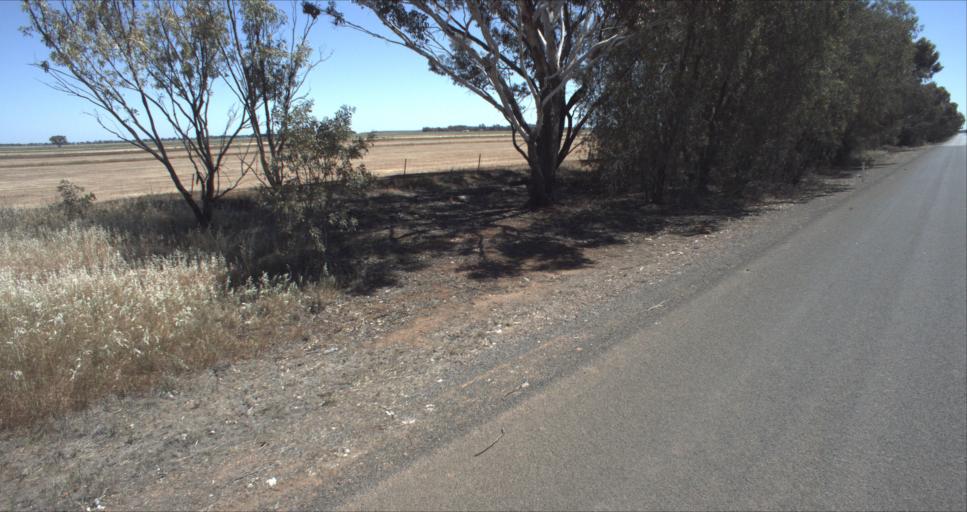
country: AU
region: New South Wales
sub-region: Leeton
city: Leeton
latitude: -34.4730
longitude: 146.2920
